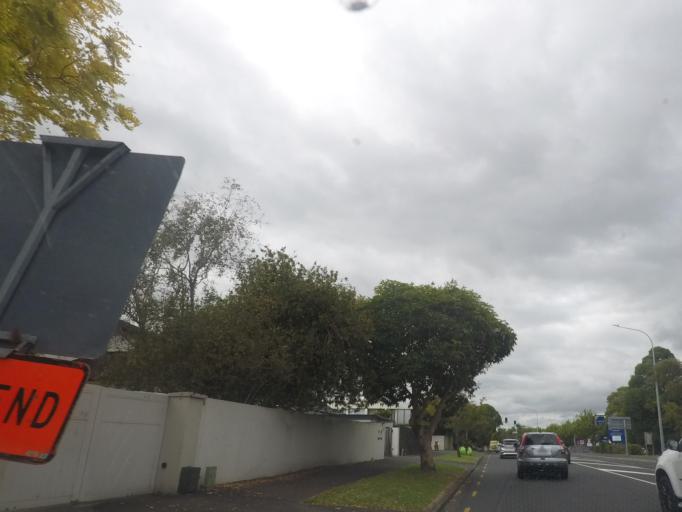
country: NZ
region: Auckland
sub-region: Auckland
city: Tamaki
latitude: -36.8604
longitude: 174.8376
